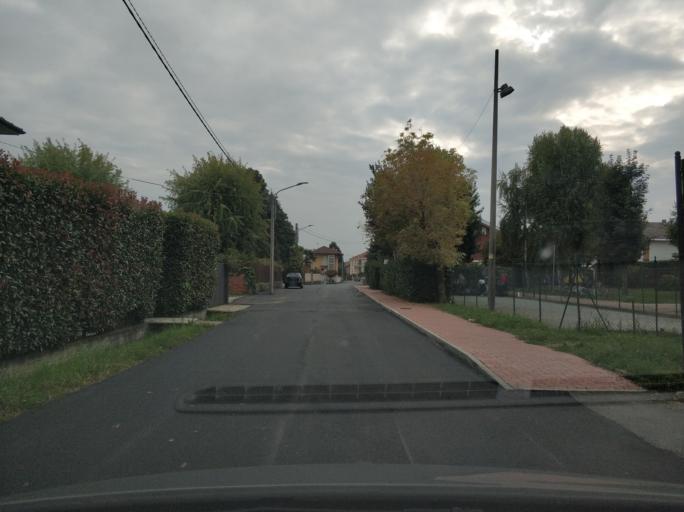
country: IT
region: Piedmont
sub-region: Provincia di Torino
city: Nole
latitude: 45.2398
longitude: 7.5705
